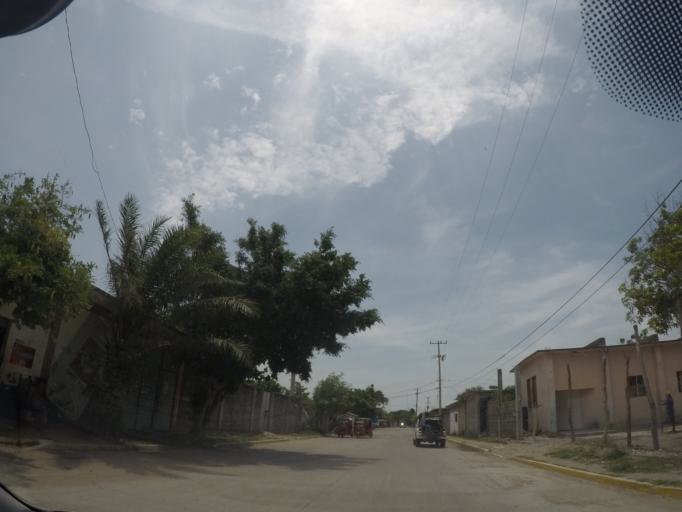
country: MX
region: Oaxaca
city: San Mateo del Mar
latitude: 16.2108
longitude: -94.9855
